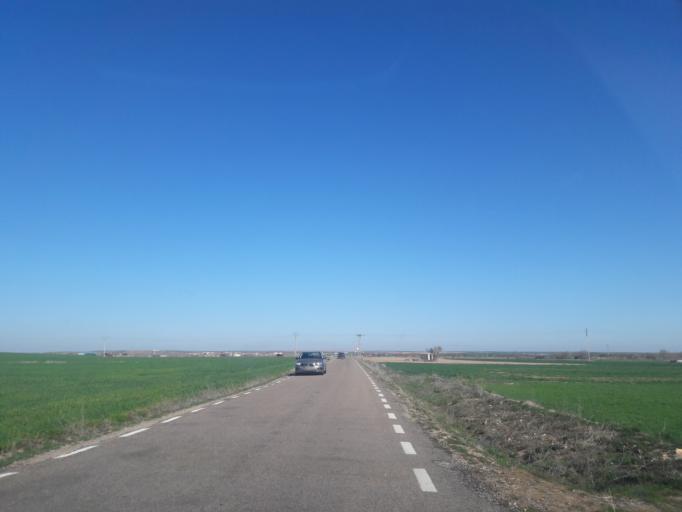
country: ES
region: Castille and Leon
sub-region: Provincia de Salamanca
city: Coca de Alba
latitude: 40.8691
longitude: -5.3750
